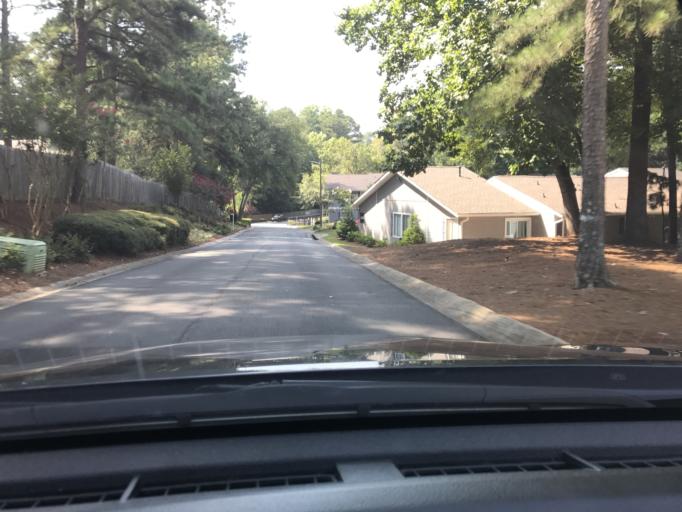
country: US
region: Georgia
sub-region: DeKalb County
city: Tucker
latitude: 33.8955
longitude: -84.2298
